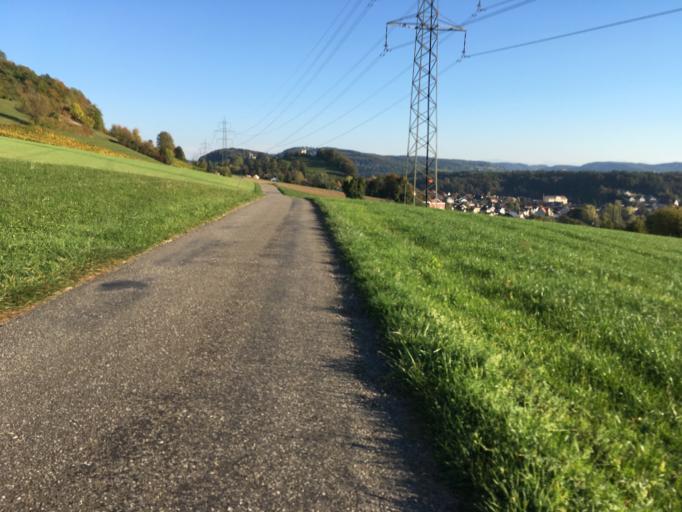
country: CH
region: Zurich
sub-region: Bezirk Buelach
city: Rorbas
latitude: 47.5411
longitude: 8.5758
